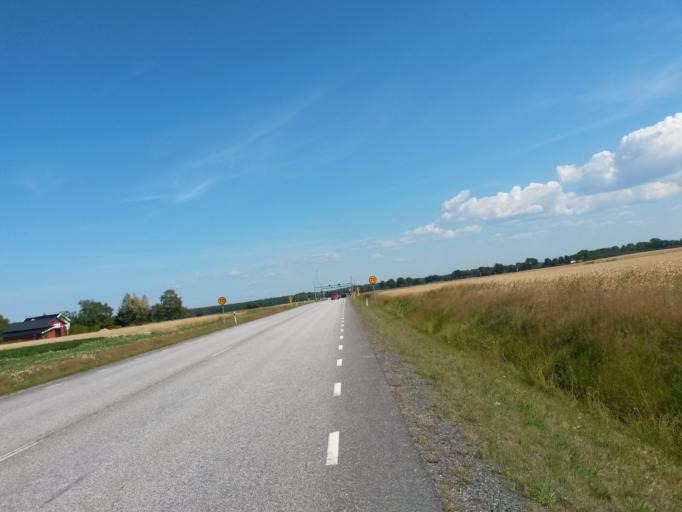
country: SE
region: Vaestra Goetaland
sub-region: Lidkopings Kommun
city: Lidkoping
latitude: 58.4811
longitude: 13.1003
